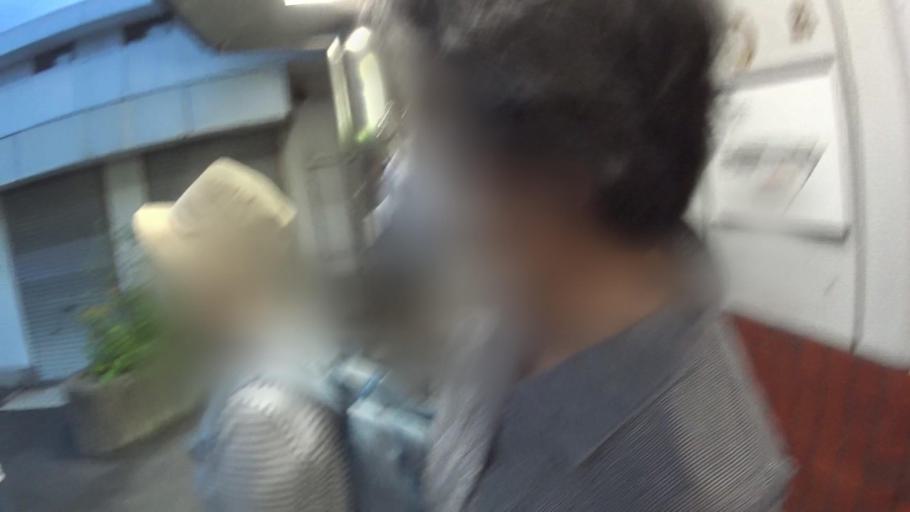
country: JP
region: Gifu
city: Tarui
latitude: 35.3069
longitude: 136.4470
